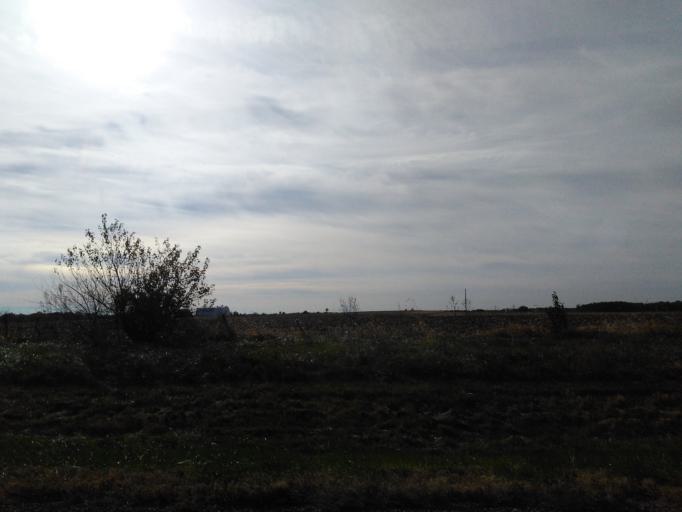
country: US
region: Illinois
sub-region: Madison County
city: Saint Jacob
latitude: 38.7629
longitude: -89.7866
